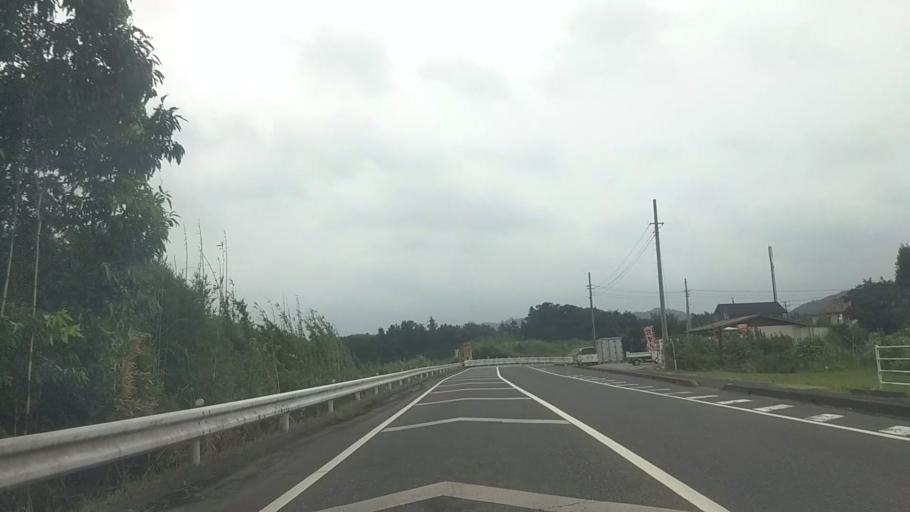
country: JP
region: Chiba
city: Kimitsu
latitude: 35.2184
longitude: 139.9177
